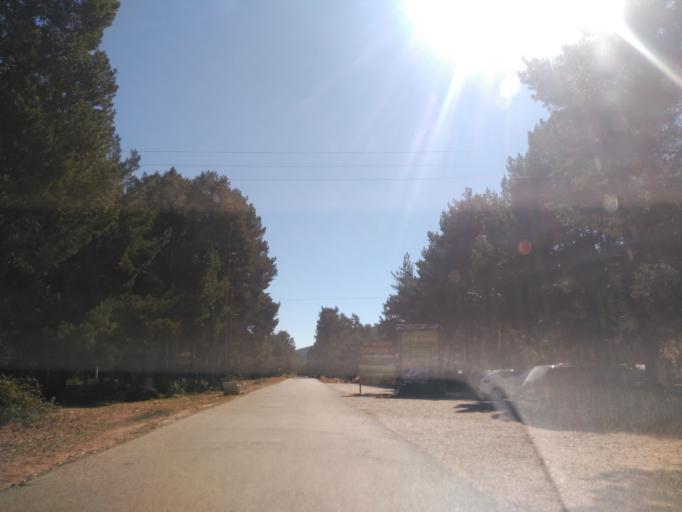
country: ES
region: Castille and Leon
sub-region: Provincia de Soria
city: Vinuesa
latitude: 41.9440
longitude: -2.7802
